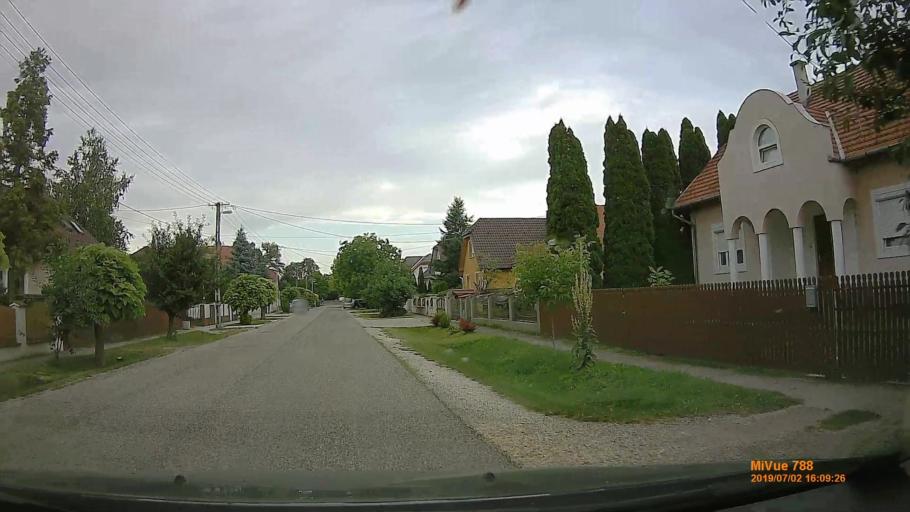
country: HU
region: Gyor-Moson-Sopron
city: Mosonmagyarovar
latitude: 47.8776
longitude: 17.2846
